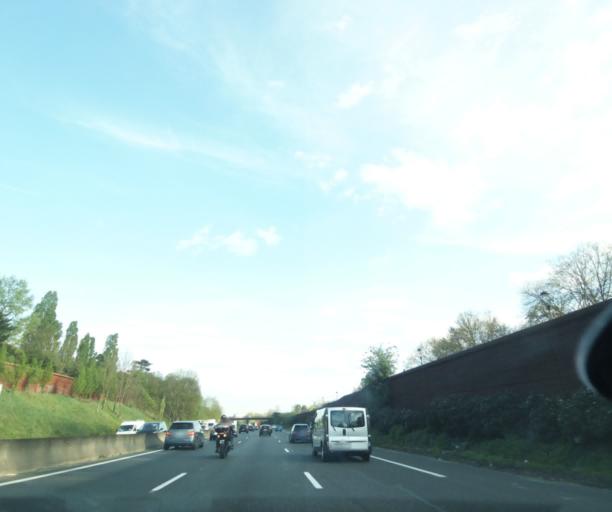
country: FR
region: Ile-de-France
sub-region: Departement de l'Essonne
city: Villemoisson-sur-Orge
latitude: 48.6835
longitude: 2.3288
